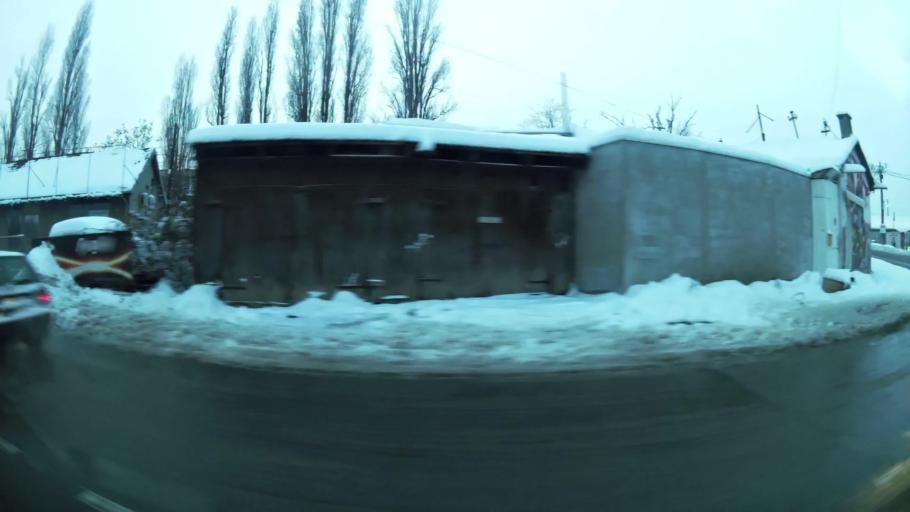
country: RS
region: Central Serbia
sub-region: Belgrade
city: Stari Grad
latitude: 44.8232
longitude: 20.4721
